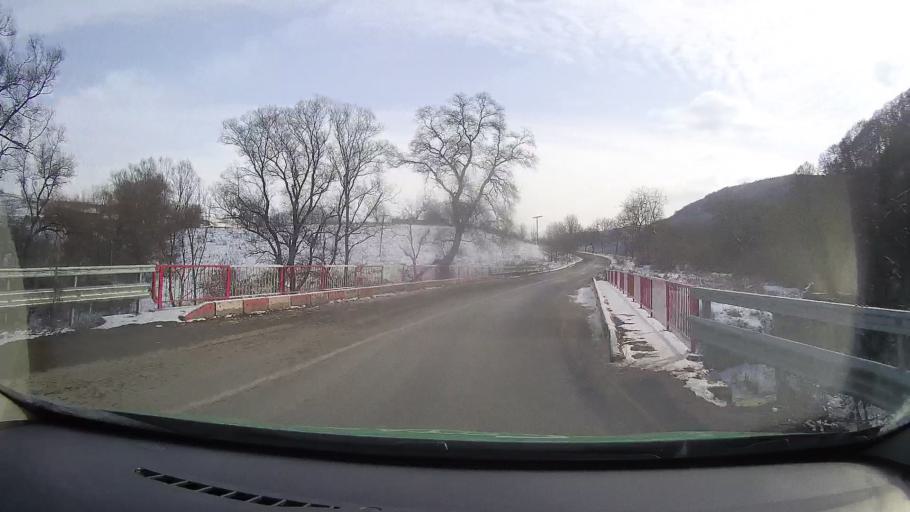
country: RO
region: Mures
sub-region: Comuna Apold
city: Saes
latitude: 46.1646
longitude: 24.7586
